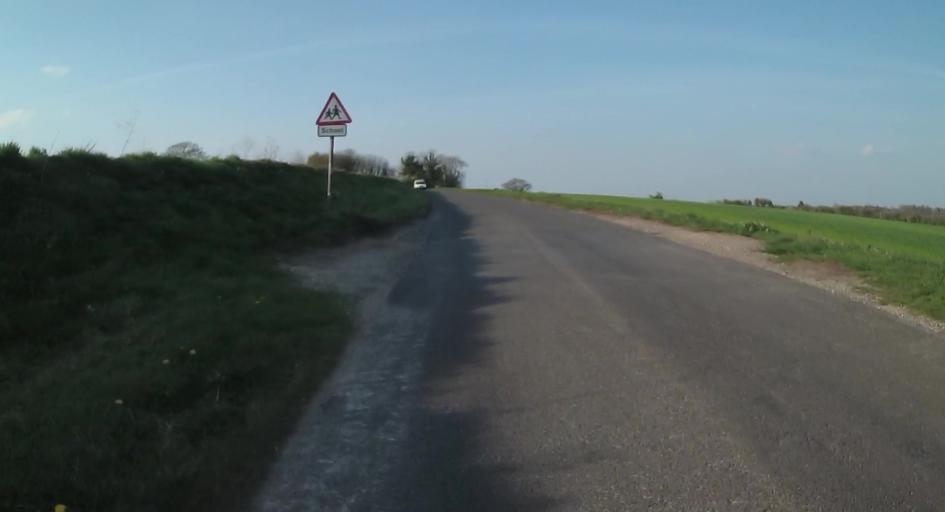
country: GB
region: England
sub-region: Hampshire
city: Basingstoke
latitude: 51.2293
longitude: -1.0918
